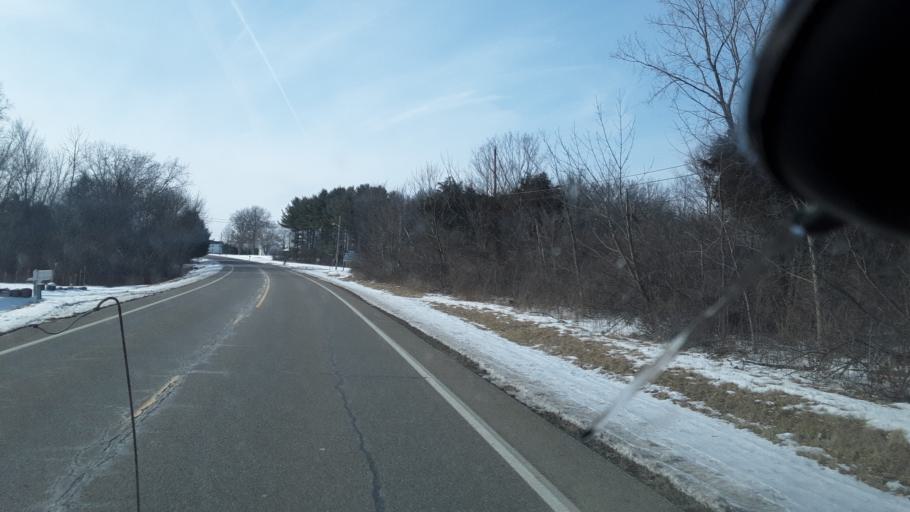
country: US
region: Ohio
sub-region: Mahoning County
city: Craig Beach
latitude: 41.0240
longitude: -81.0103
